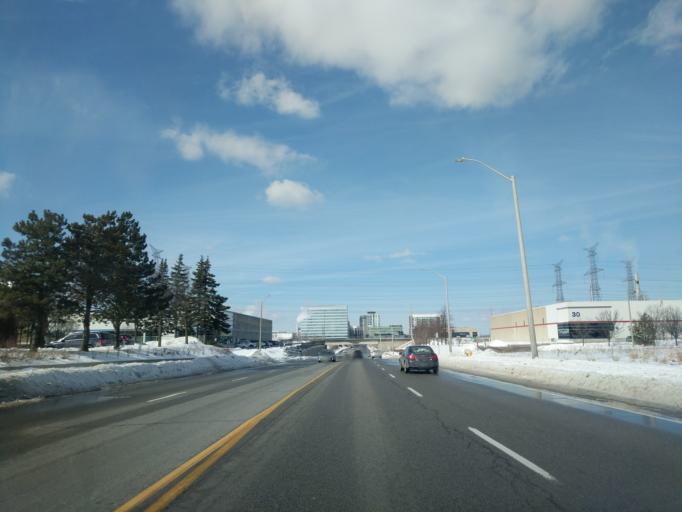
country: CA
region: Ontario
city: Markham
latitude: 43.8415
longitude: -79.3211
